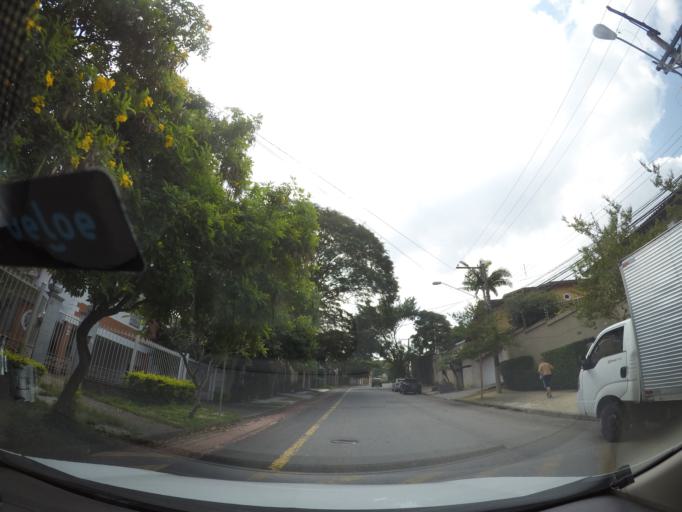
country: BR
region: Sao Paulo
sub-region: Sao Paulo
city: Sao Paulo
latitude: -23.6024
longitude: -46.7030
